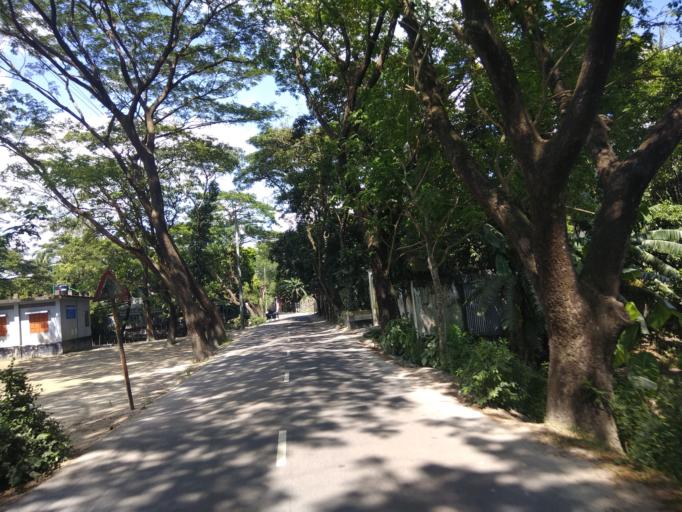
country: BD
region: Dhaka
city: Narayanganj
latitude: 23.4396
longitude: 90.4895
